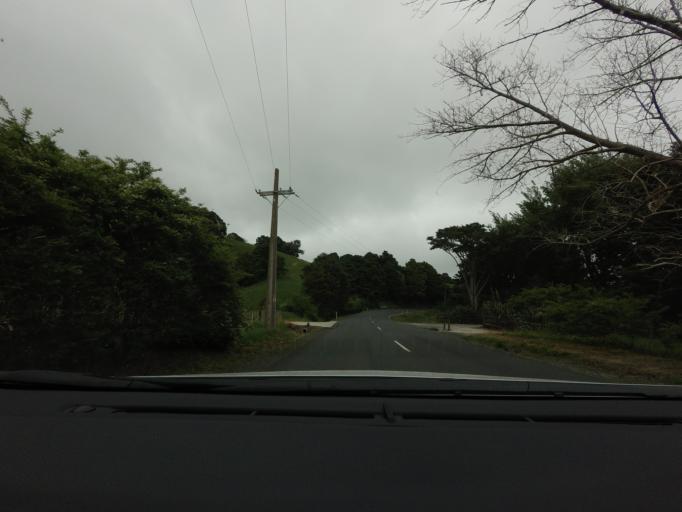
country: NZ
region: Auckland
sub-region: Auckland
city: Wellsford
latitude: -36.2817
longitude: 174.6002
